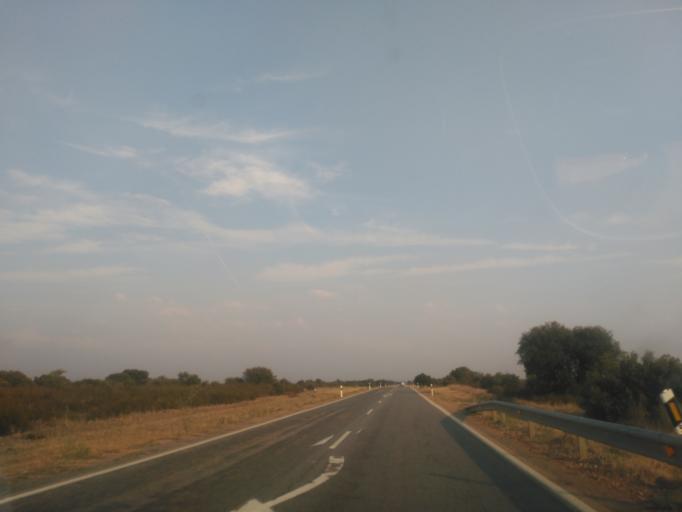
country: ES
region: Castille and Leon
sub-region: Provincia de Zamora
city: Perilla de Castro
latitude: 41.7330
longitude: -5.8248
